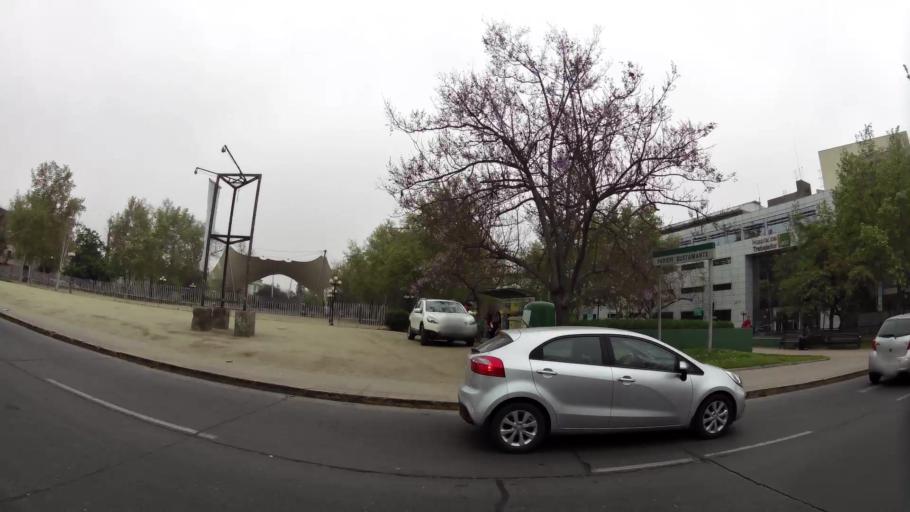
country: CL
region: Santiago Metropolitan
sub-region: Provincia de Santiago
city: Santiago
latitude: -33.4428
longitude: -70.6318
